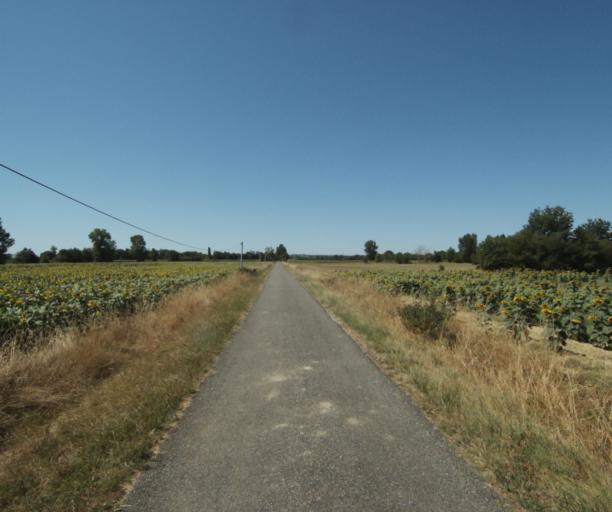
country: FR
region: Midi-Pyrenees
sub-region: Departement de la Haute-Garonne
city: Revel
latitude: 43.4925
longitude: 1.9622
